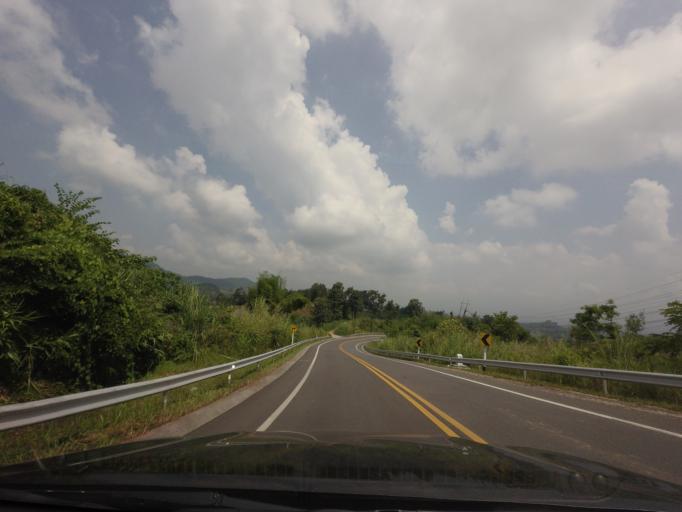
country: TH
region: Nan
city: Santi Suk
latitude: 18.9176
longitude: 100.8859
